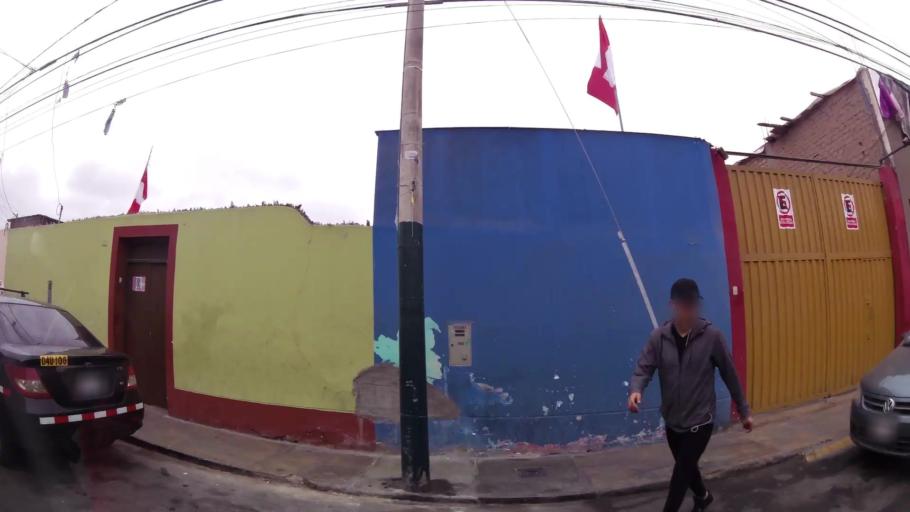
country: PE
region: Lima
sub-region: Lima
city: Surco
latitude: -12.1445
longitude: -77.0028
